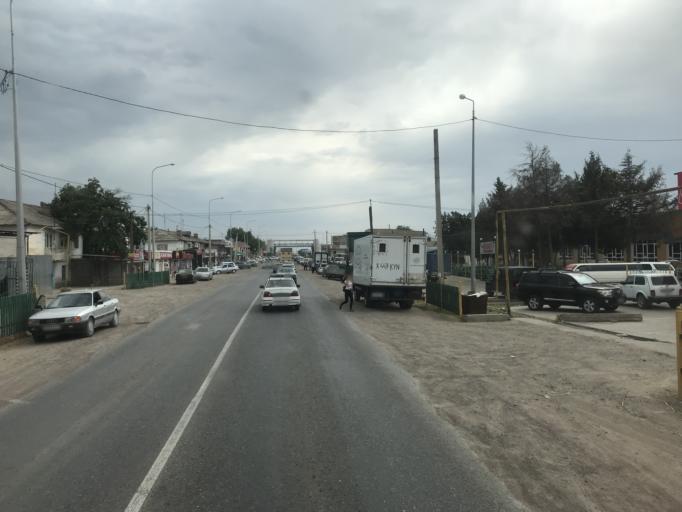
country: KZ
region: Ongtustik Qazaqstan
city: Saryaghash
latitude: 41.3416
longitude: 68.9535
